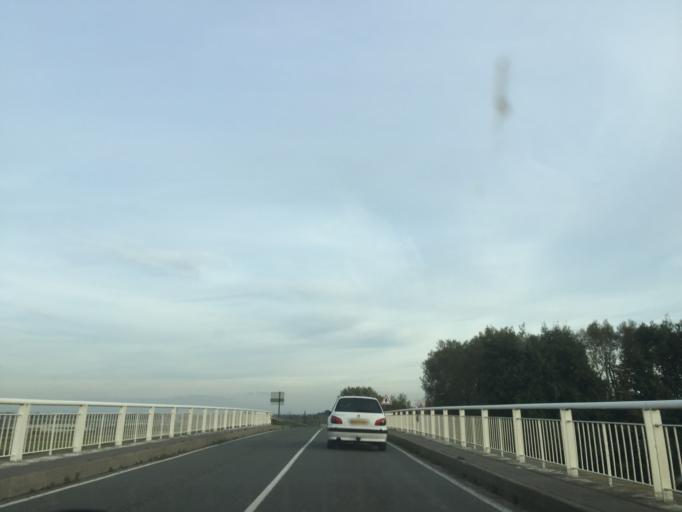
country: FR
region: Nord-Pas-de-Calais
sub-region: Departement du Pas-de-Calais
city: Coquelles
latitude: 50.9148
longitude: 1.7865
